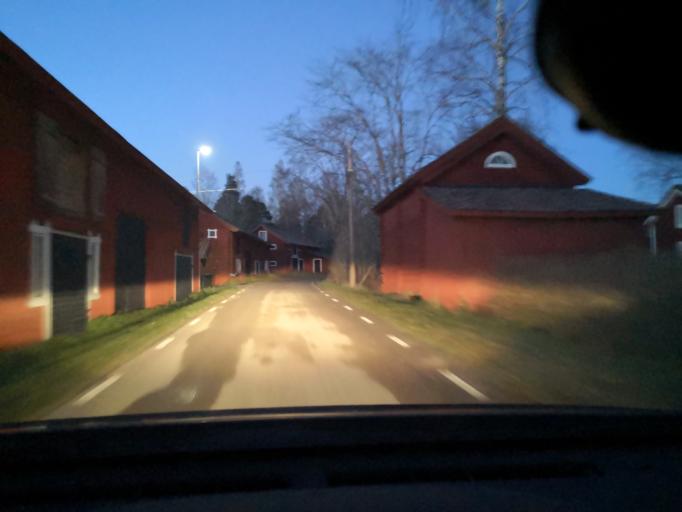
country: SE
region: Vaestmanland
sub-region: Sala Kommun
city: Sala
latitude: 59.8726
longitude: 16.7219
